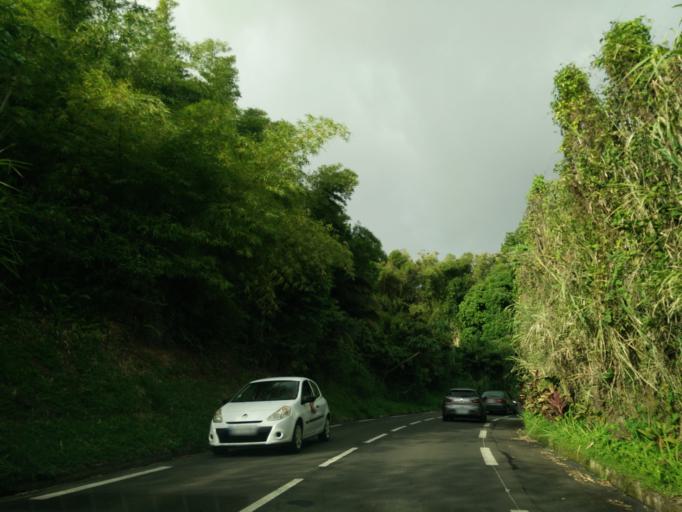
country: MQ
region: Martinique
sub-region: Martinique
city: Le Morne-Rouge
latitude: 14.7627
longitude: -61.1554
